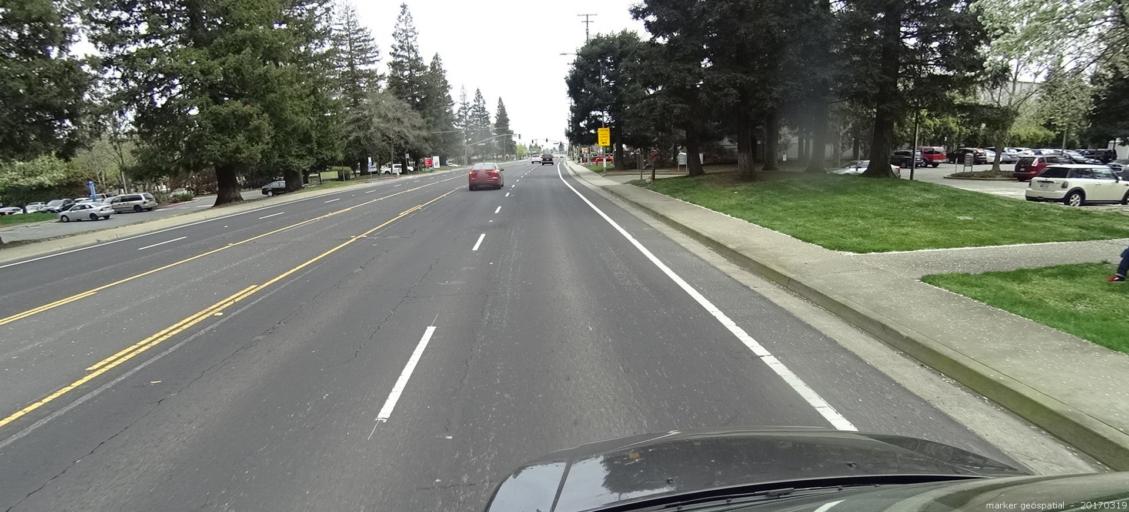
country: US
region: California
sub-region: Sacramento County
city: Rosemont
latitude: 38.5506
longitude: -121.4144
